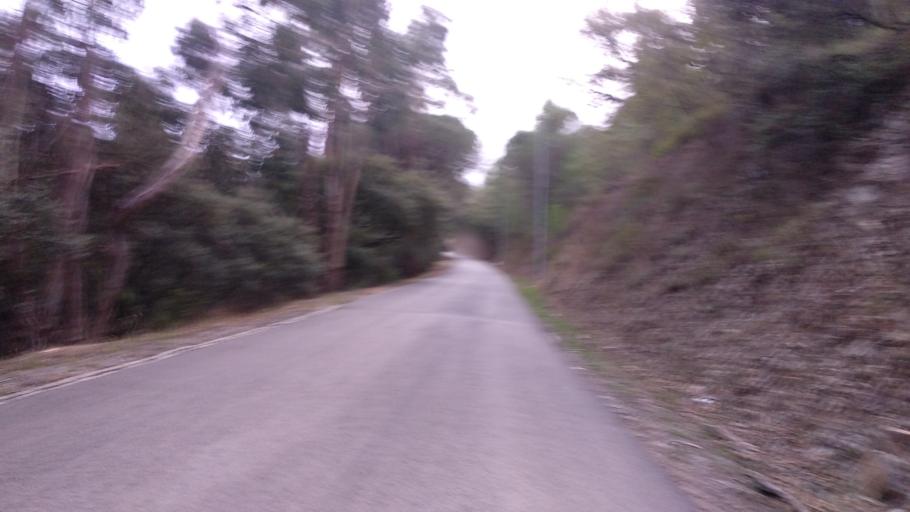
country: PT
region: Faro
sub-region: Sao Bras de Alportel
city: Sao Bras de Alportel
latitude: 37.1827
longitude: -7.9136
